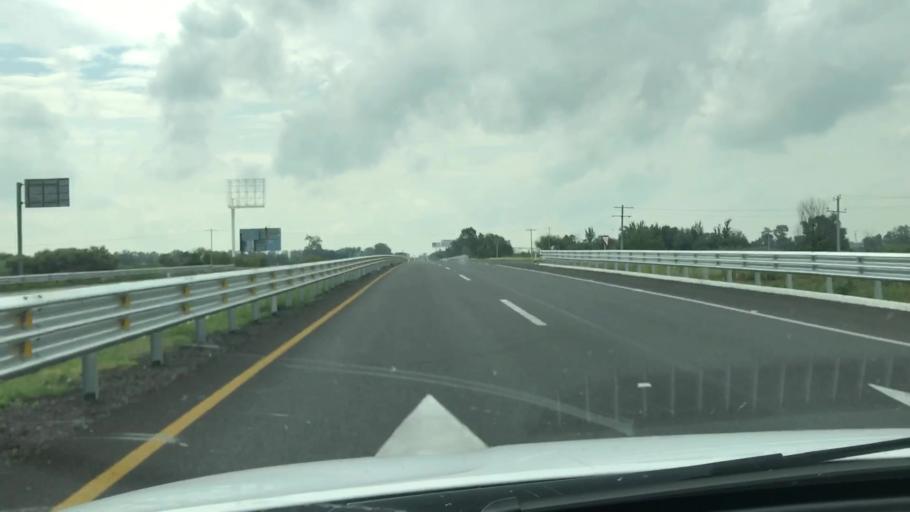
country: MX
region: Guanajuato
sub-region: Irapuato
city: Cuarta Brigada
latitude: 20.6541
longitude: -101.2884
